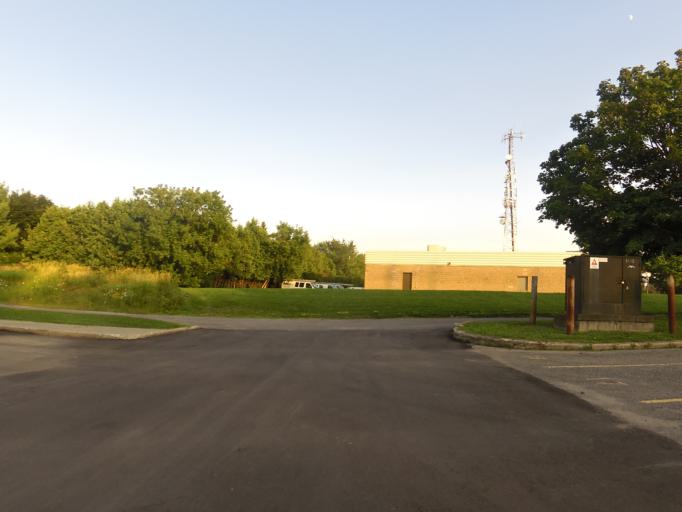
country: CA
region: Ontario
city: Bells Corners
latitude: 45.3277
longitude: -75.8340
